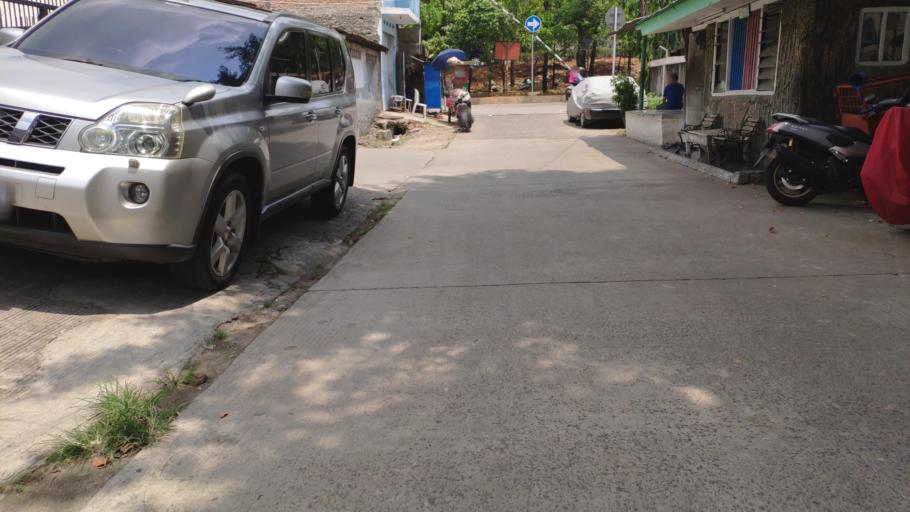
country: ID
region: Jakarta Raya
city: Jakarta
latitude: -6.2123
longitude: 106.8734
